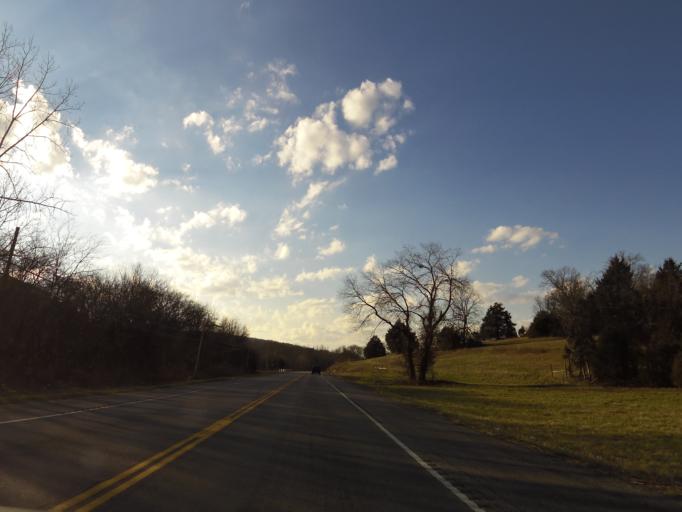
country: US
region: Tennessee
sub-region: Smith County
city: Carthage
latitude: 36.2533
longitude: -86.0409
